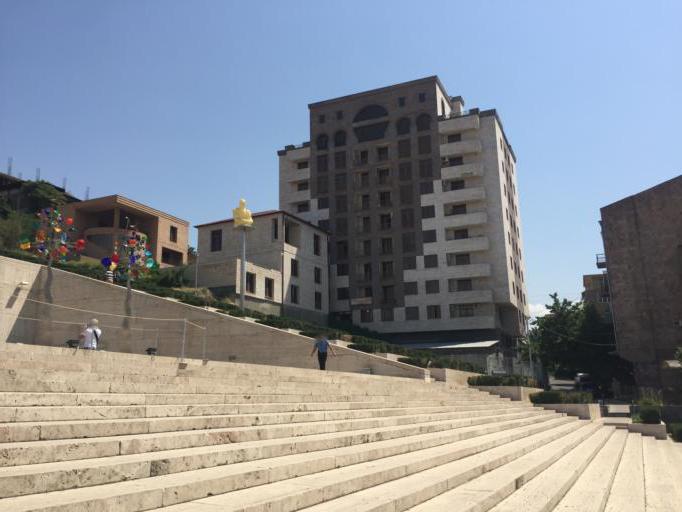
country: AM
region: Yerevan
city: Yerevan
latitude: 40.1905
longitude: 44.5154
